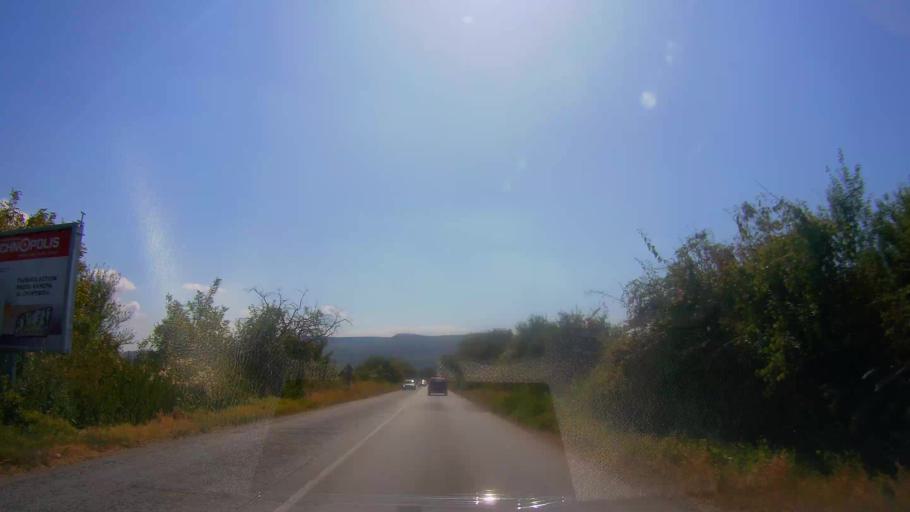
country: BG
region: Veliko Turnovo
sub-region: Obshtina Gorna Oryakhovitsa
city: Purvomaytsi
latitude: 43.1640
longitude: 25.6182
